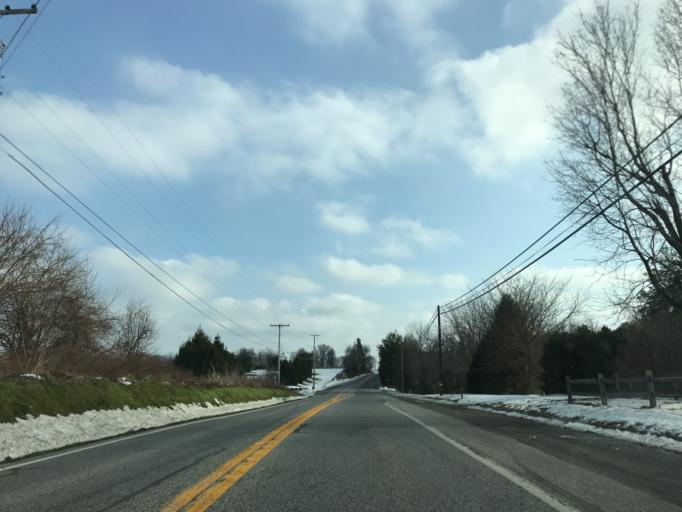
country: US
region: Maryland
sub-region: Harford County
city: South Bel Air
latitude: 39.5700
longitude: -76.2545
